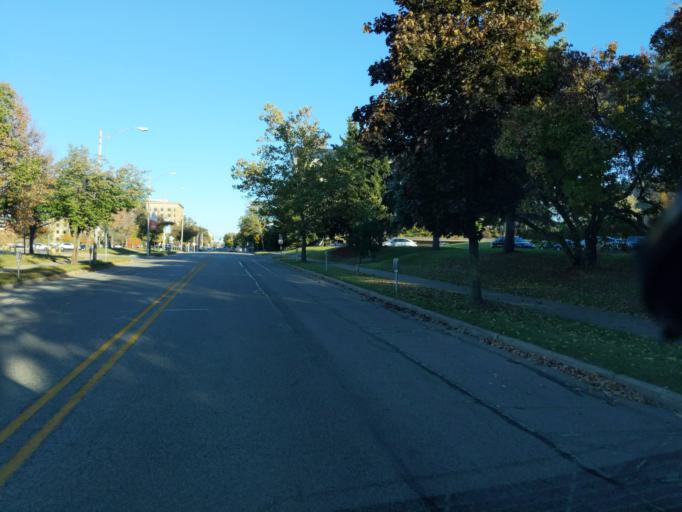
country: US
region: Michigan
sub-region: Ingham County
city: Lansing
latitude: 42.7300
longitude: -84.5630
